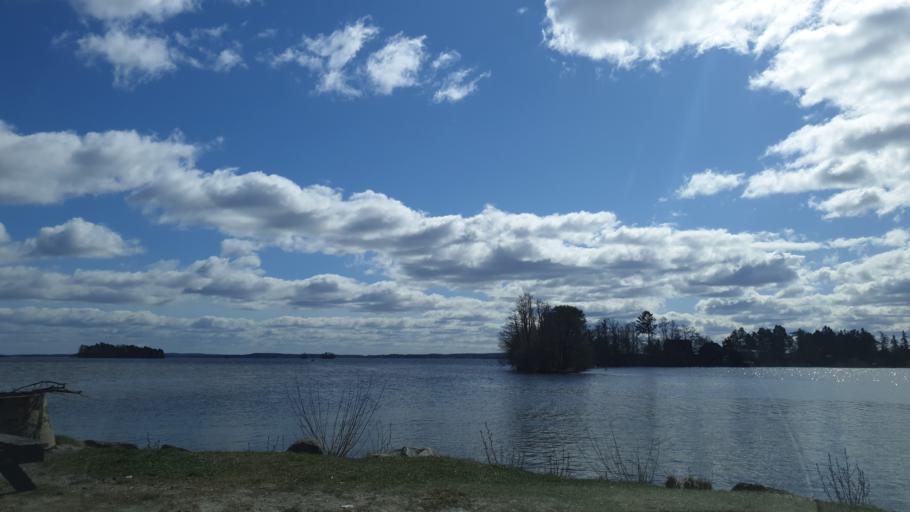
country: SE
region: Vaestmanland
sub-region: Kungsors Kommun
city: Kungsoer
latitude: 59.4716
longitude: 16.0700
